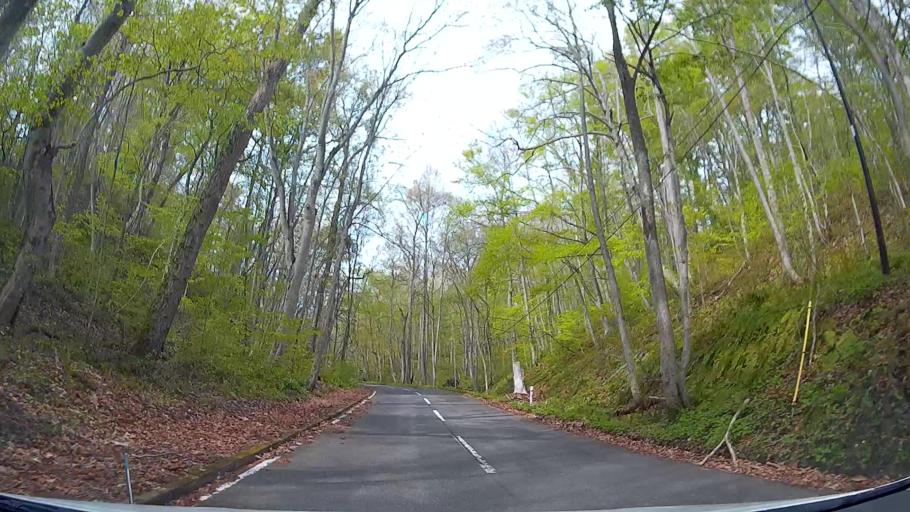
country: JP
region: Akita
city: Hanawa
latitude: 40.4266
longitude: 140.9120
